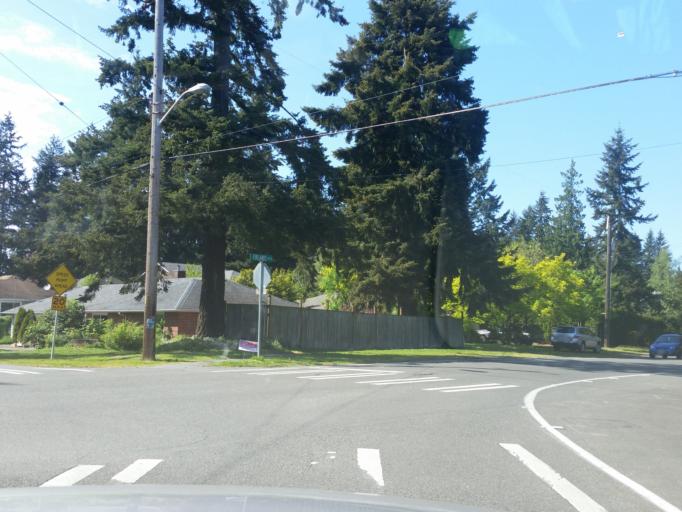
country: US
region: Washington
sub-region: King County
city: Shoreline
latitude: 47.7651
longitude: -122.3485
